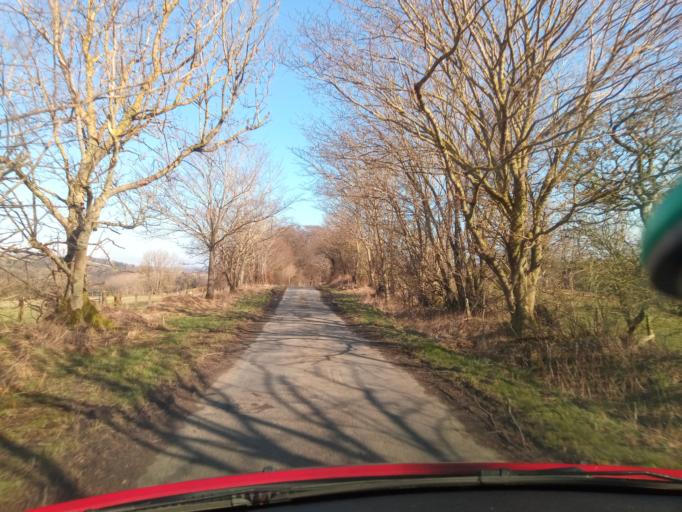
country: GB
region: Scotland
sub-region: The Scottish Borders
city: Hawick
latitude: 55.5023
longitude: -2.7685
